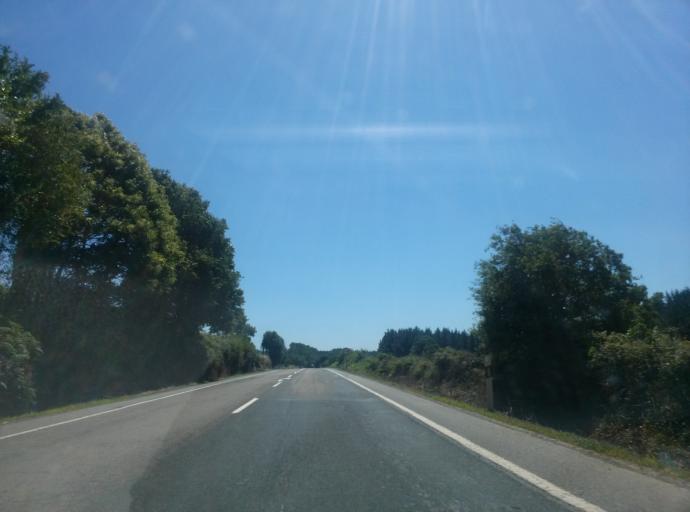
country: ES
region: Galicia
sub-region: Provincia de Lugo
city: Castro de Rei
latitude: 43.1226
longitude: -7.4260
